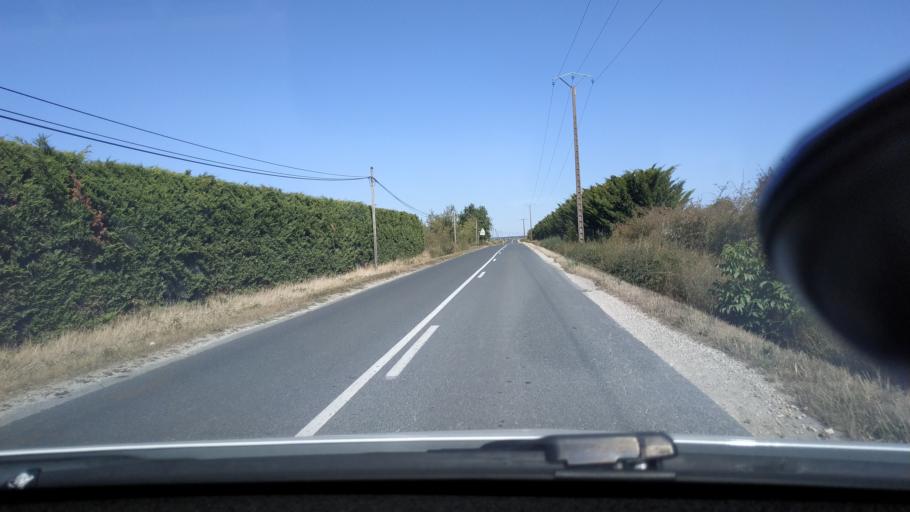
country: FR
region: Centre
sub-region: Departement du Loiret
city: Poilly-lez-Gien
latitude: 47.6627
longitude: 2.5724
